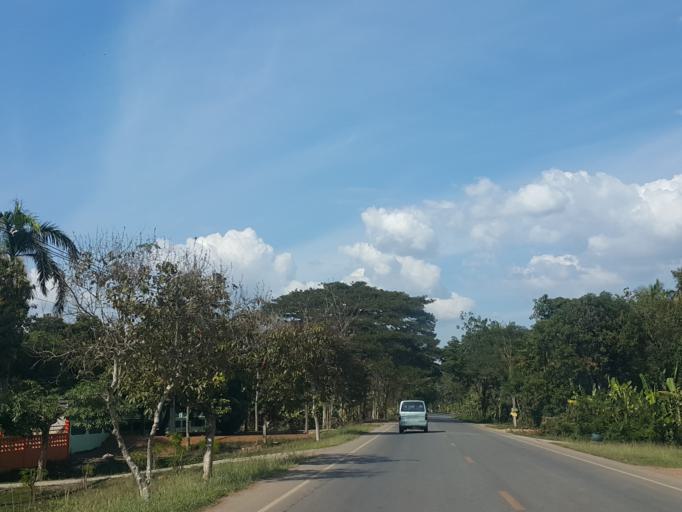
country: TH
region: Sukhothai
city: Sawankhalok
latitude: 17.2736
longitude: 99.8302
